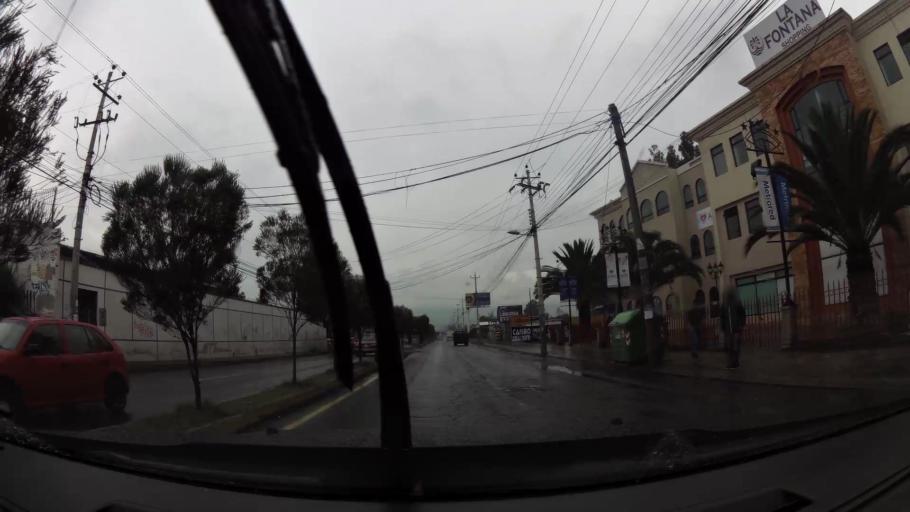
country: EC
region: Pichincha
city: Sangolqui
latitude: -0.3096
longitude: -78.4442
